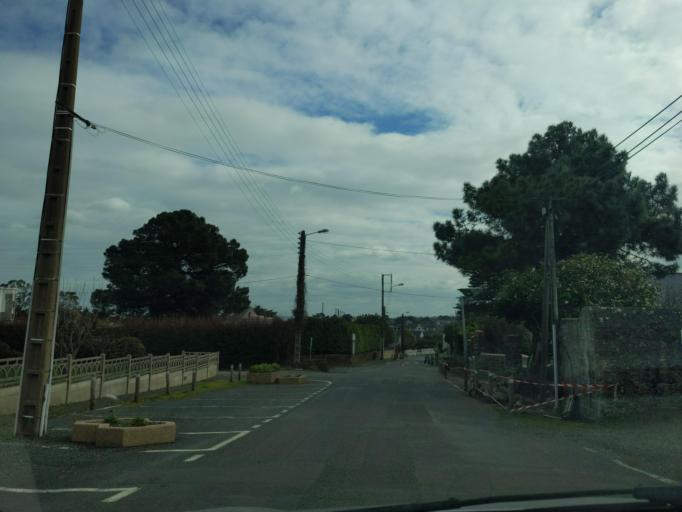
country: FR
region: Brittany
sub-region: Departement des Cotes-d'Armor
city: Saint-Quay-Portrieux
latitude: 48.6625
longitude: -2.8458
